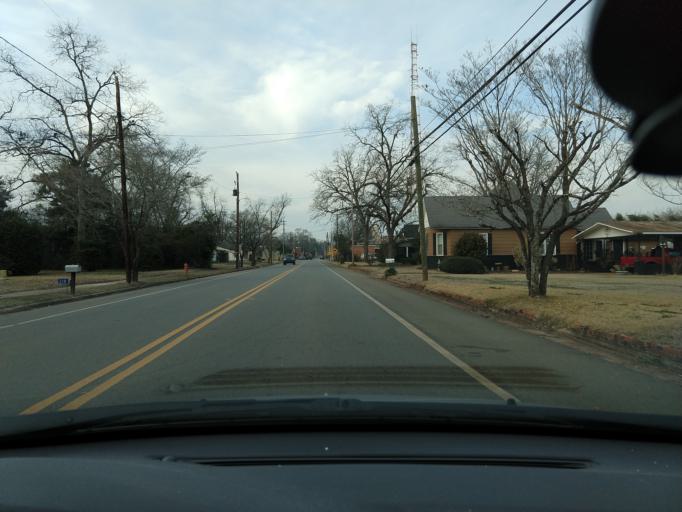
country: US
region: Georgia
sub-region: Webster County
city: Preston
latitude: 32.0312
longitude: -84.3915
